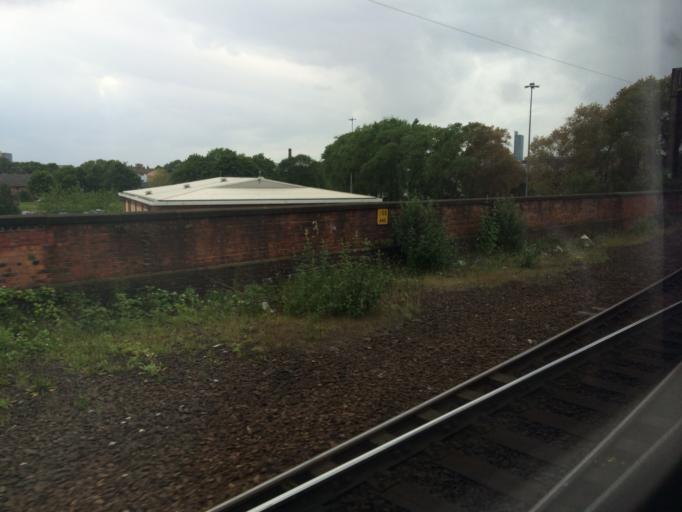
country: GB
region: England
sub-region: Manchester
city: Manchester
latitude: 53.4739
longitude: -2.2199
